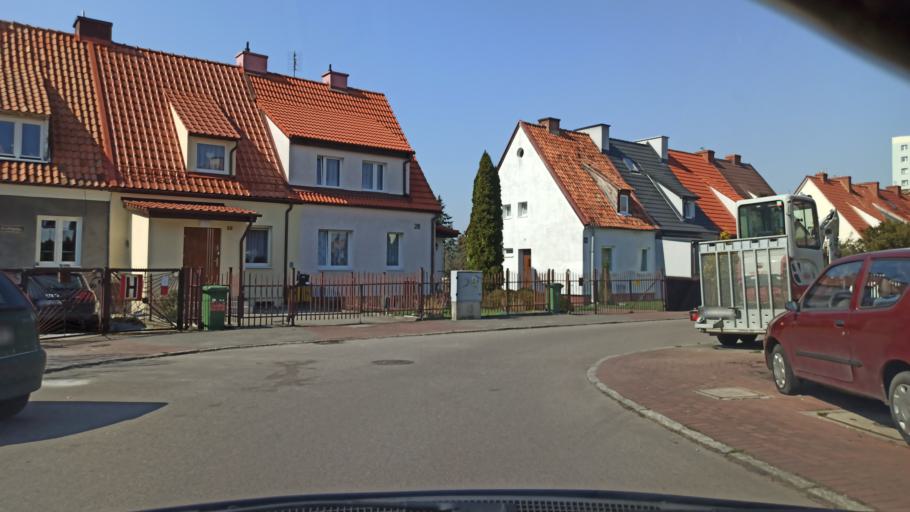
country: PL
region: Warmian-Masurian Voivodeship
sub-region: Powiat elblaski
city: Elblag
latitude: 54.1445
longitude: 19.4049
